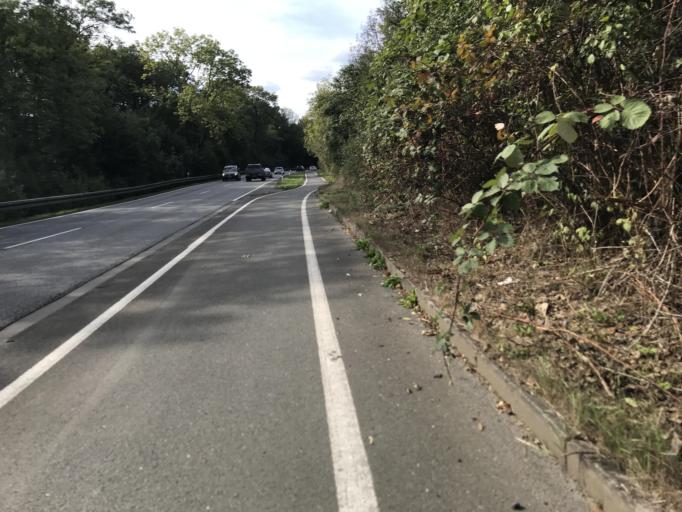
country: DE
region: Hesse
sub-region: Regierungsbezirk Giessen
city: Asslar
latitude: 50.5930
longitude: 8.4438
